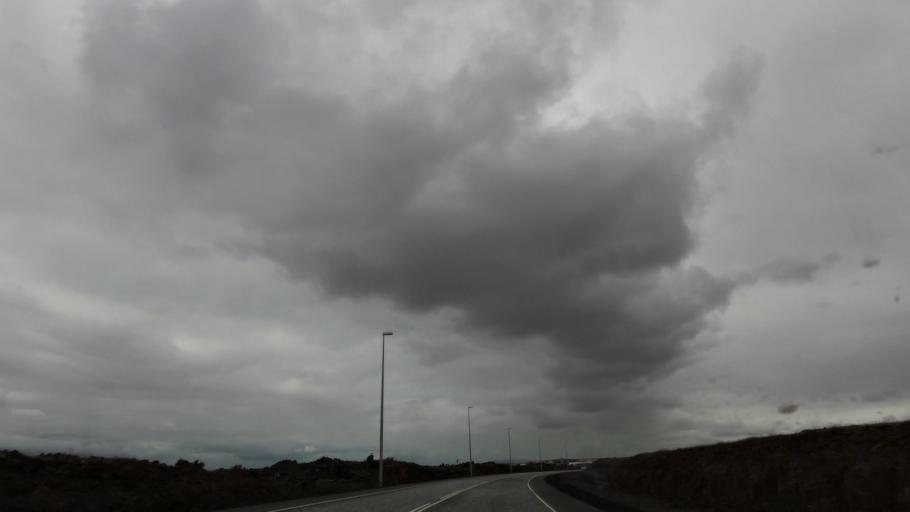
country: IS
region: Capital Region
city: Hafnarfjoerdur
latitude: 64.0908
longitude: -21.9732
